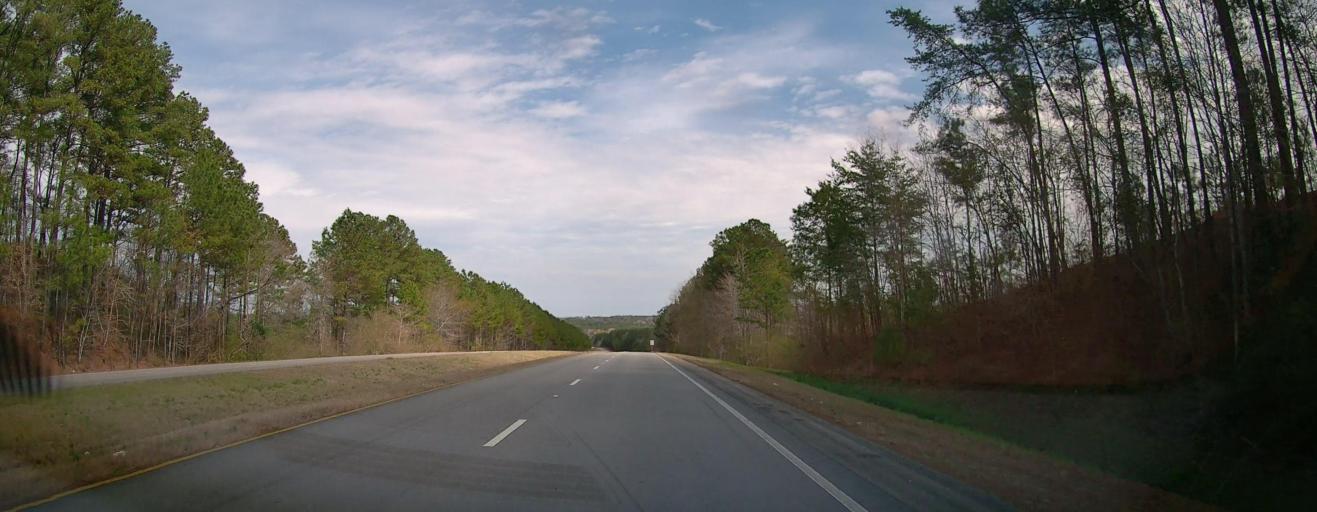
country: US
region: Alabama
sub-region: Marion County
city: Winfield
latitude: 33.9315
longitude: -87.6970
